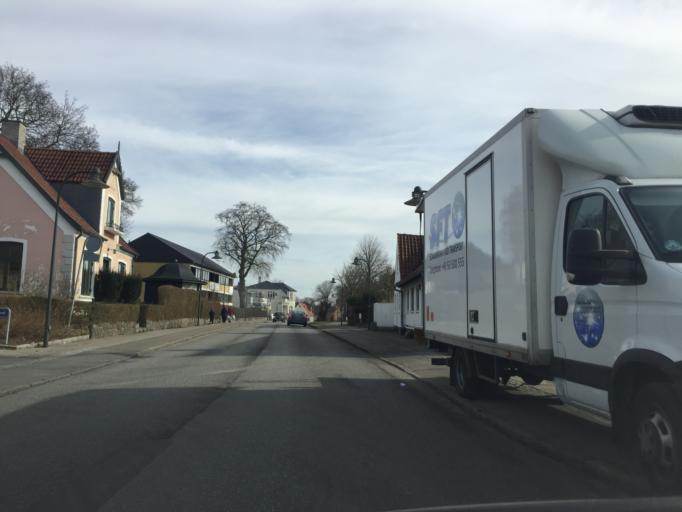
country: DK
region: Capital Region
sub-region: Fureso Kommune
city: Farum
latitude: 55.8083
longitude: 12.3589
